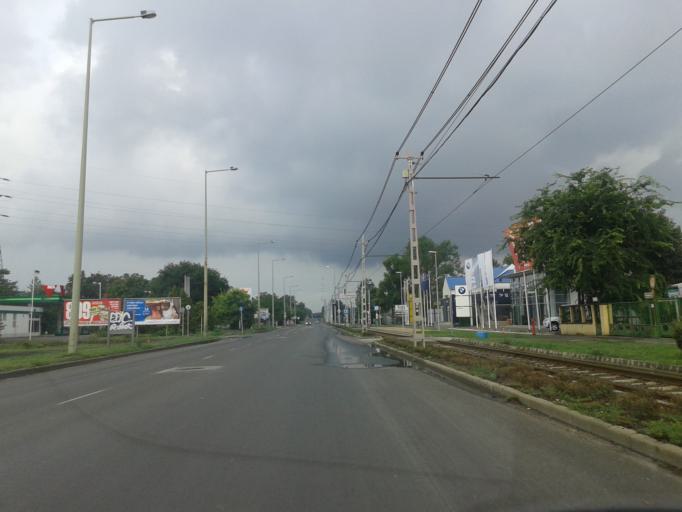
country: HU
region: Csongrad
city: Szeged
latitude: 46.2539
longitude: 20.1206
